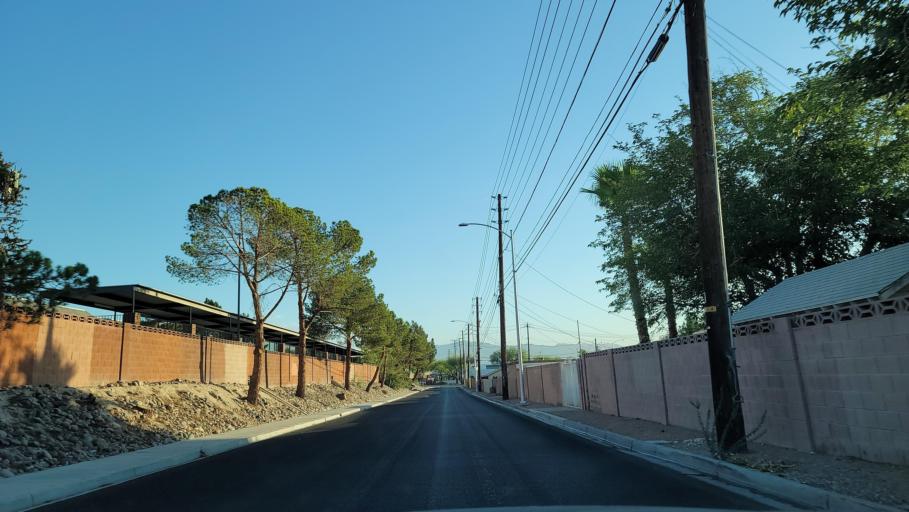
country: US
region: Nevada
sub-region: Clark County
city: Las Vegas
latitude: 36.1572
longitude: -115.1907
